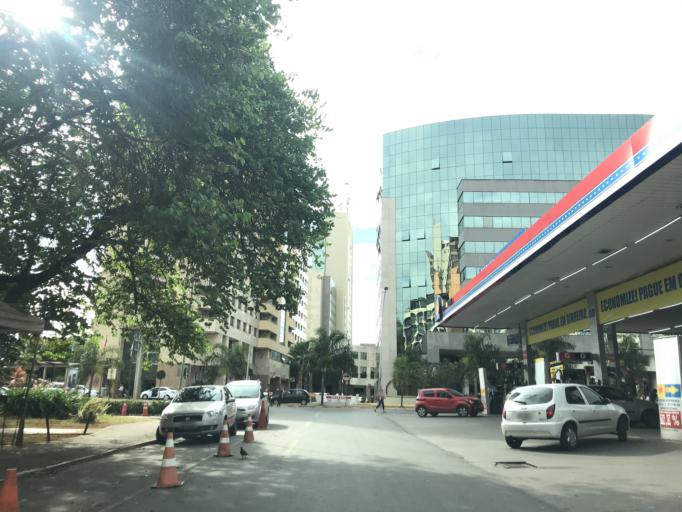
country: BR
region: Federal District
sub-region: Brasilia
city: Brasilia
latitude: -15.7937
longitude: -47.8923
